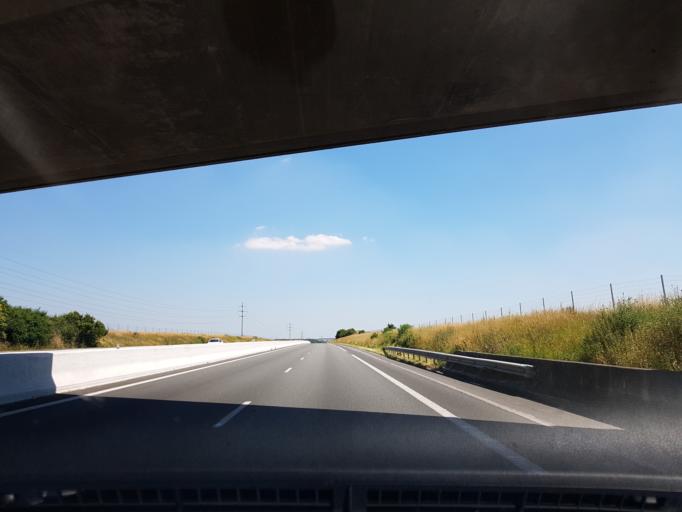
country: FR
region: Nord-Pas-de-Calais
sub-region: Departement du Nord
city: Iwuy
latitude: 50.2352
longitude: 3.2862
